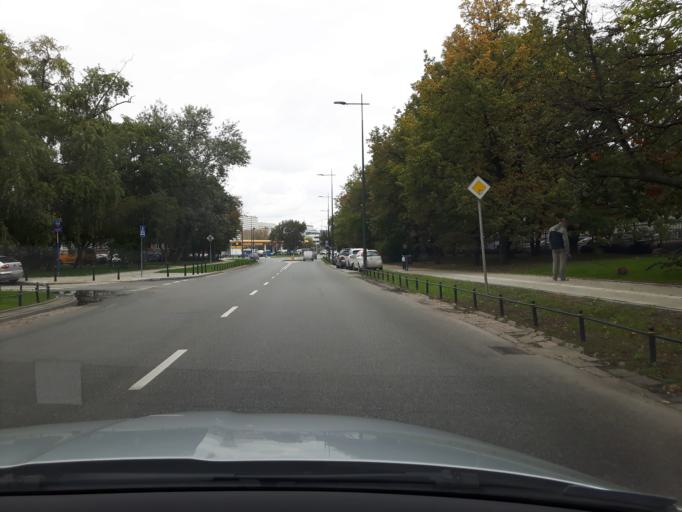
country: PL
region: Masovian Voivodeship
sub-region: Warszawa
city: Mokotow
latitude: 52.1759
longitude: 21.0086
